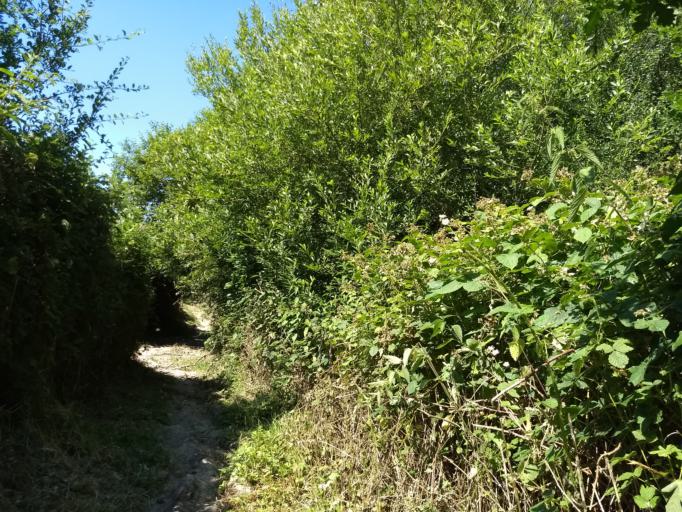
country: GB
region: England
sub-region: Isle of Wight
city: Gurnard
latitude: 50.7322
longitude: -1.3622
